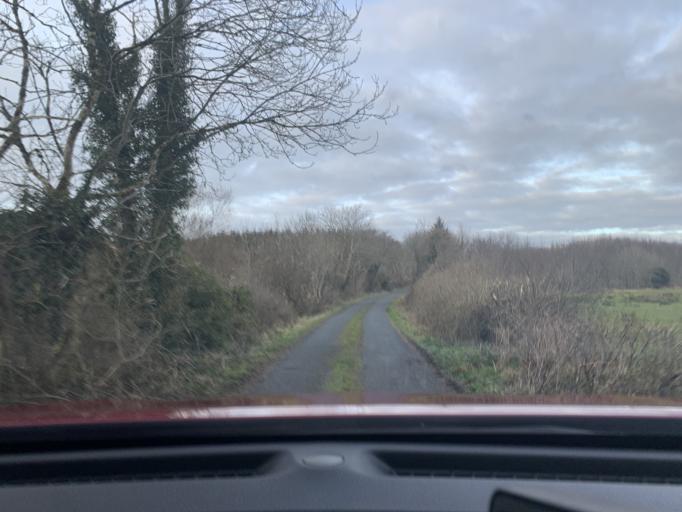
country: IE
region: Connaught
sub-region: Sligo
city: Ballymote
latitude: 54.0066
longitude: -8.5761
